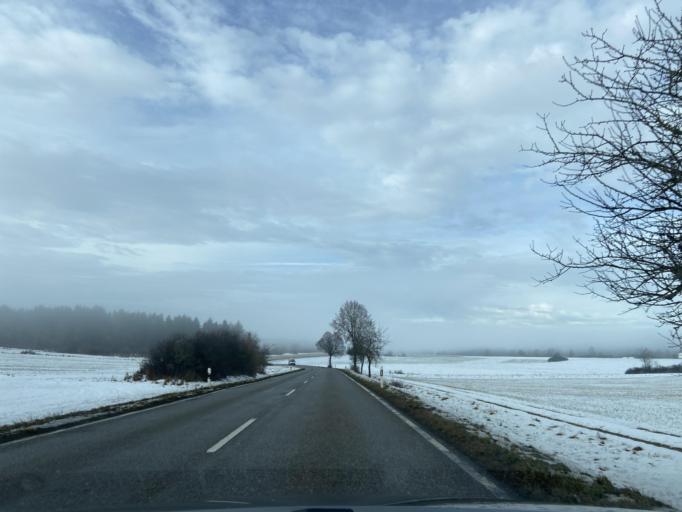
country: DE
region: Baden-Wuerttemberg
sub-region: Tuebingen Region
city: Gammertingen
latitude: 48.2407
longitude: 9.2513
